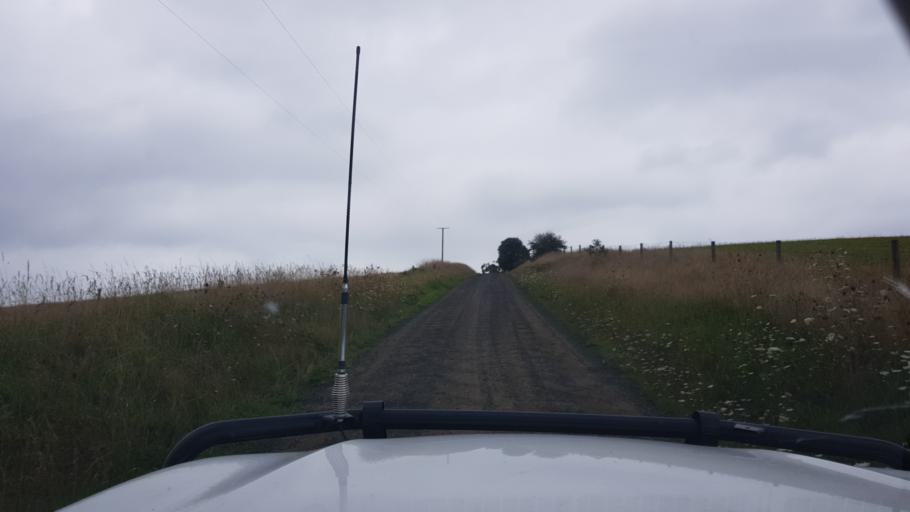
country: AU
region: Victoria
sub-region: Baw Baw
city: Warragul
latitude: -38.0882
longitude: 145.9521
